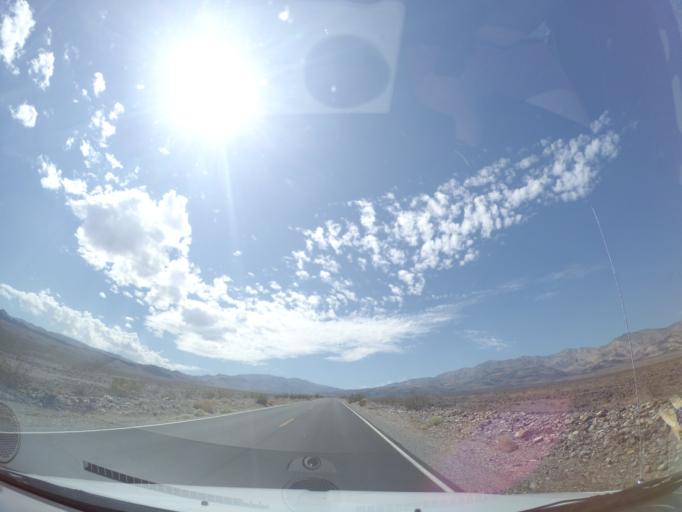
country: US
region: Nevada
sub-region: Nye County
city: Beatty
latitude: 36.5268
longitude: -117.2201
